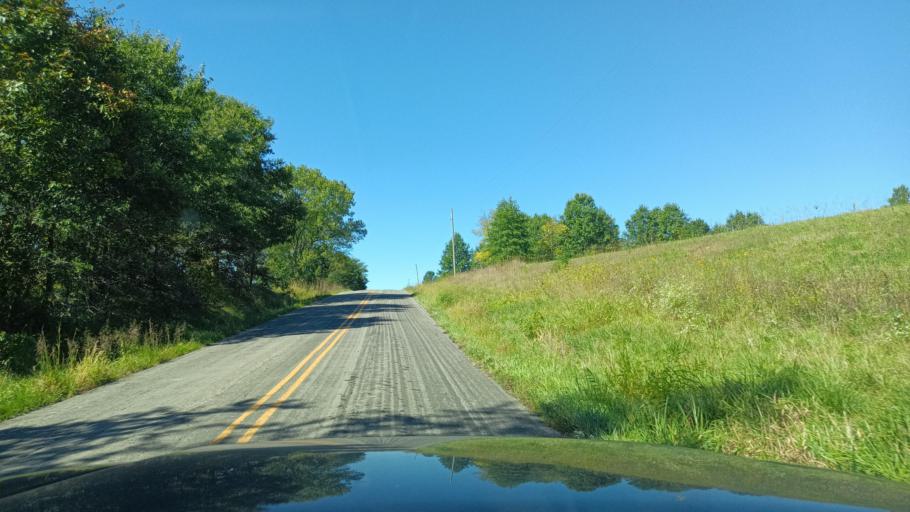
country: US
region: Missouri
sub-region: Scotland County
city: Memphis
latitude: 40.3543
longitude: -92.2799
